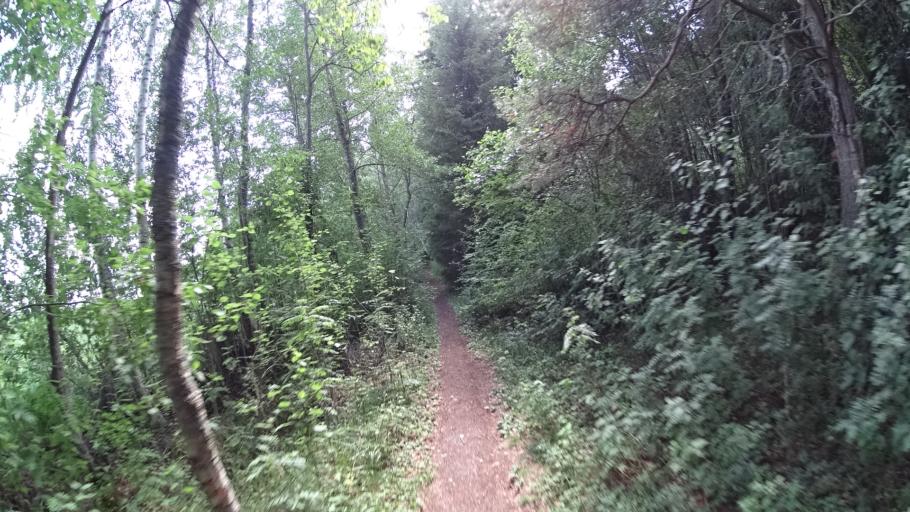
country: FI
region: Haeme
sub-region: Forssa
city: Tammela
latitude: 60.7740
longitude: 23.8657
